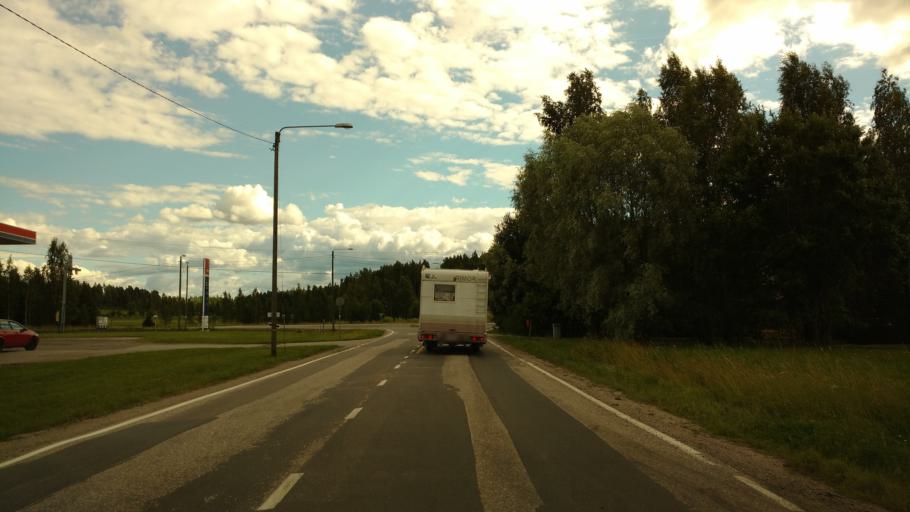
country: FI
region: Varsinais-Suomi
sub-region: Salo
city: Halikko
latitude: 60.3841
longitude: 23.0419
